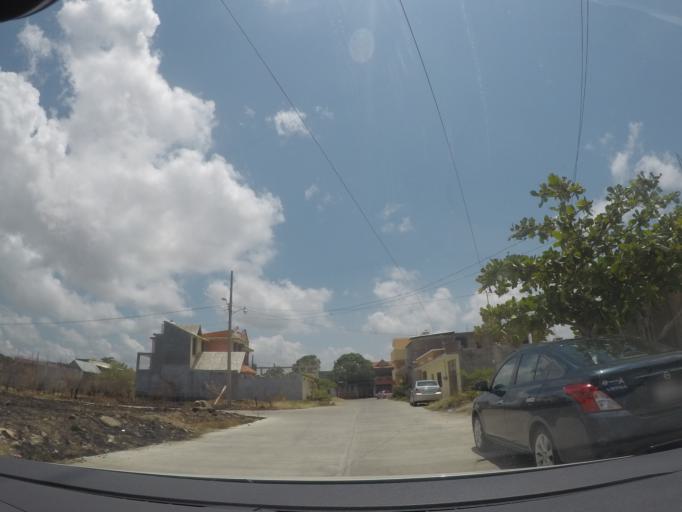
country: MX
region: Oaxaca
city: Juchitan de Zaragoza
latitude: 16.4423
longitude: -95.0106
